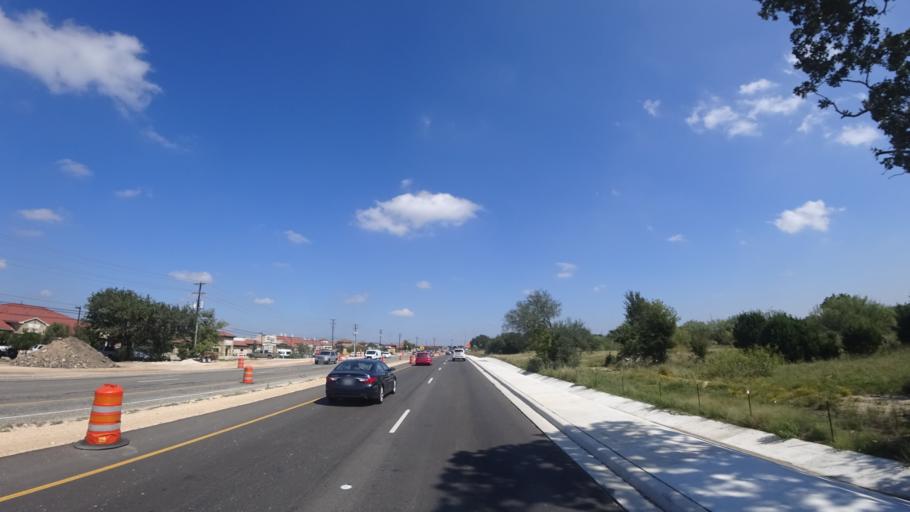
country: US
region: Texas
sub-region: Williamson County
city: Round Rock
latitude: 30.5114
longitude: -97.7063
